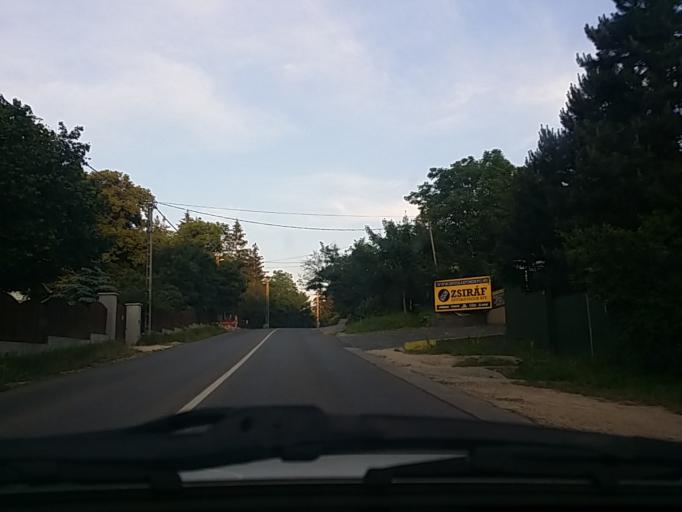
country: HU
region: Pest
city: Solymar
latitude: 47.5735
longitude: 18.9428
